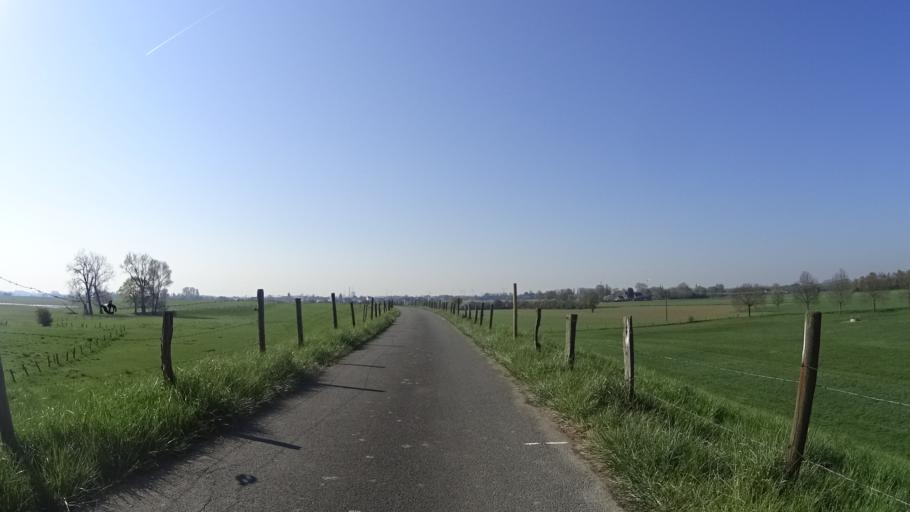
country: DE
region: North Rhine-Westphalia
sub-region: Regierungsbezirk Dusseldorf
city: Alpen
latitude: 51.6083
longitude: 6.5729
